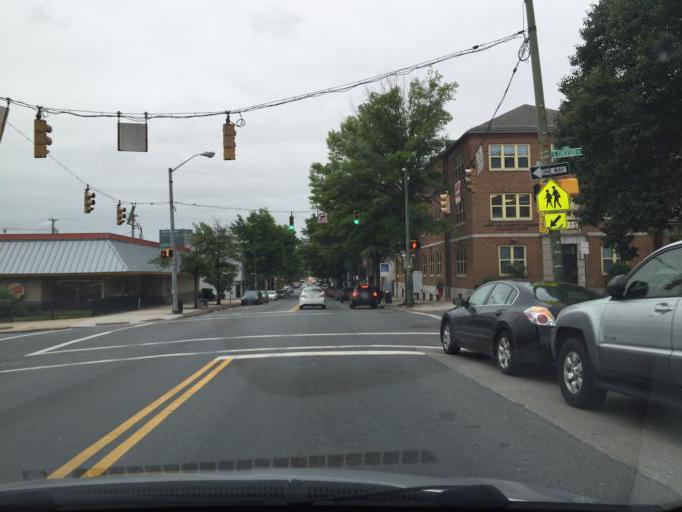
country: US
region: Maryland
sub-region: City of Baltimore
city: Baltimore
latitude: 39.2859
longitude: -76.5868
